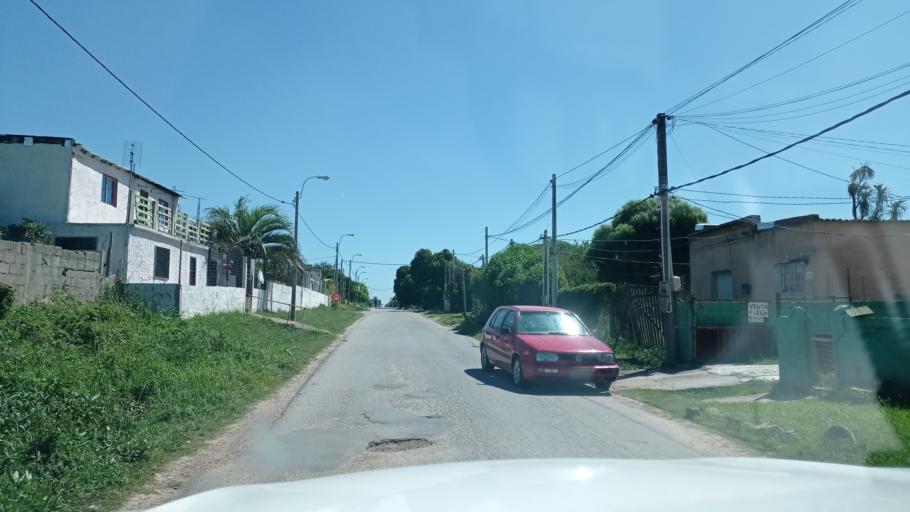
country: UY
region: Montevideo
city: Montevideo
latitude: -34.8687
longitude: -56.2698
